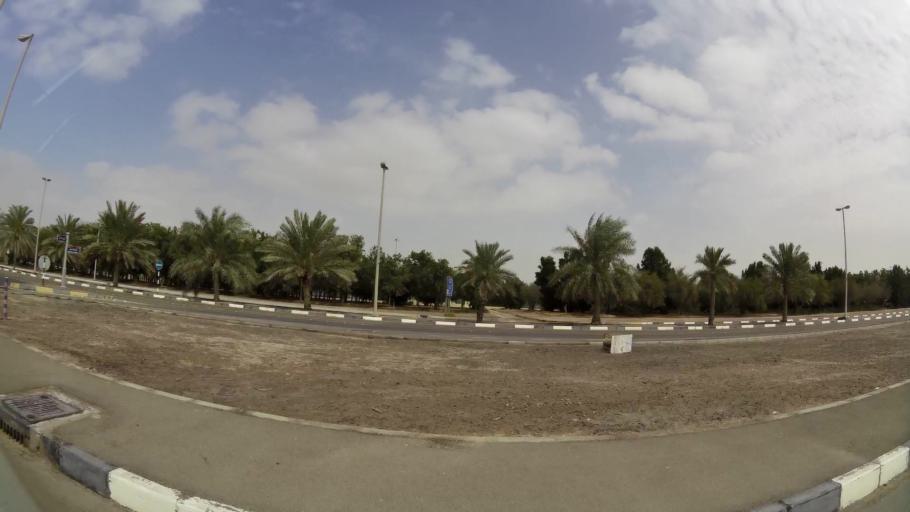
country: AE
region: Abu Dhabi
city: Abu Dhabi
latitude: 24.3959
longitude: 54.5057
